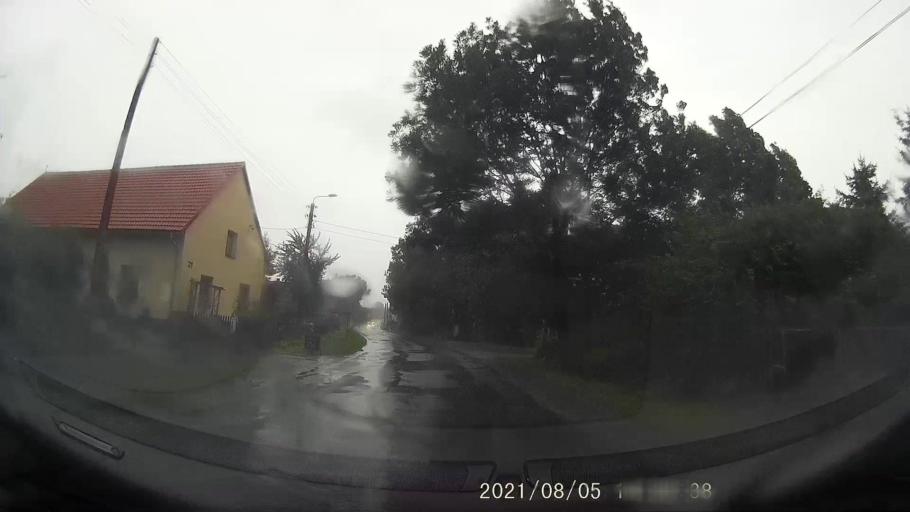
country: PL
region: Opole Voivodeship
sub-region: Powiat nyski
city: Korfantow
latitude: 50.4782
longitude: 17.6548
